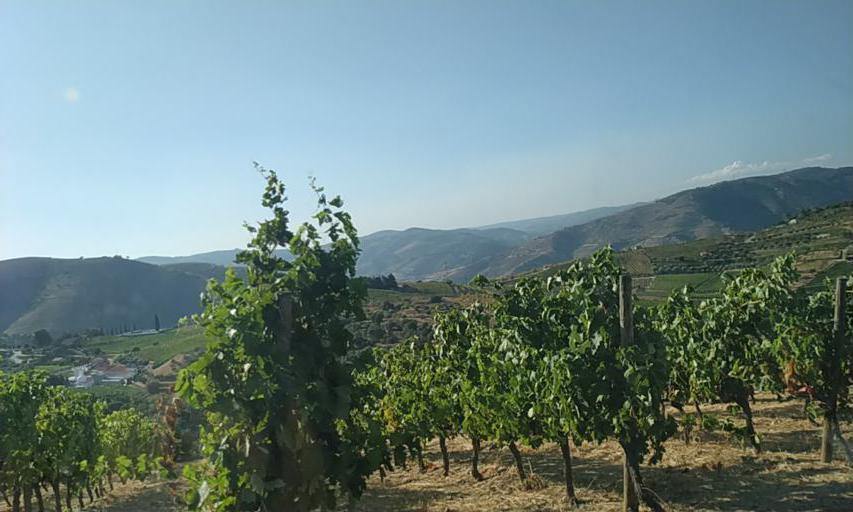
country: PT
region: Viseu
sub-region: Sao Joao da Pesqueira
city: Sao Joao da Pesqueira
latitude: 41.1834
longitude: -7.4022
